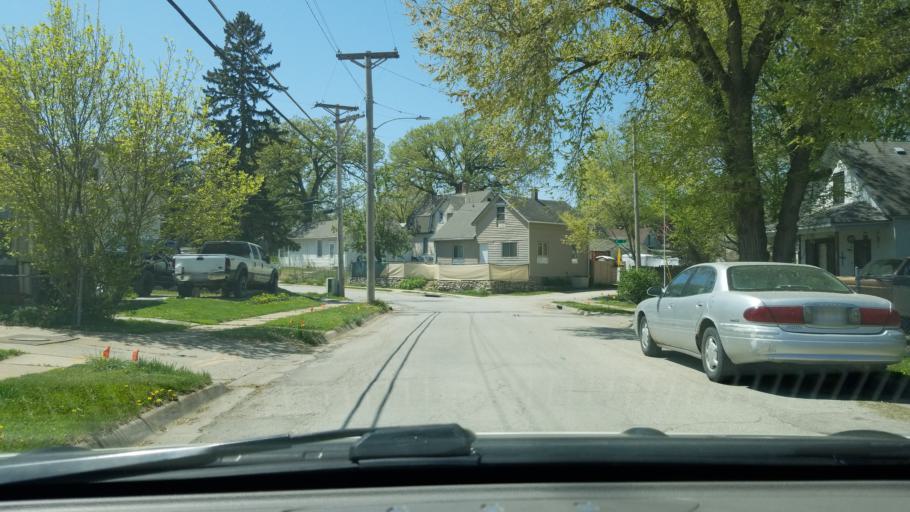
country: US
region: Nebraska
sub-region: Douglas County
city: Omaha
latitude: 41.2251
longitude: -95.9392
